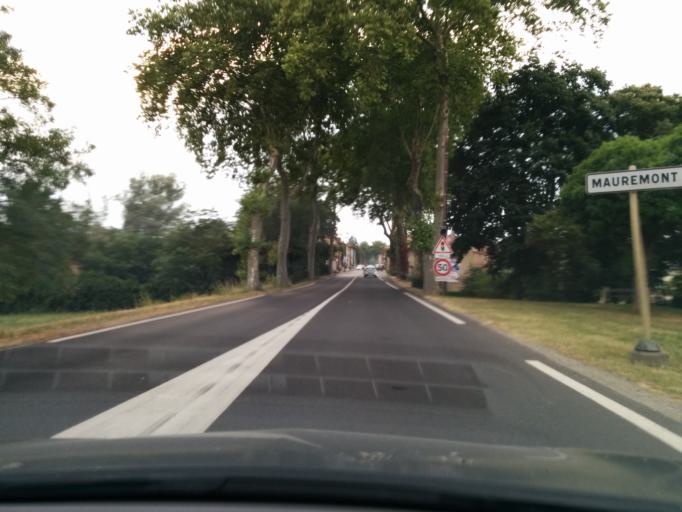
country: FR
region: Midi-Pyrenees
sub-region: Departement de la Haute-Garonne
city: Villenouvelle
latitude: 43.4343
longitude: 1.6647
